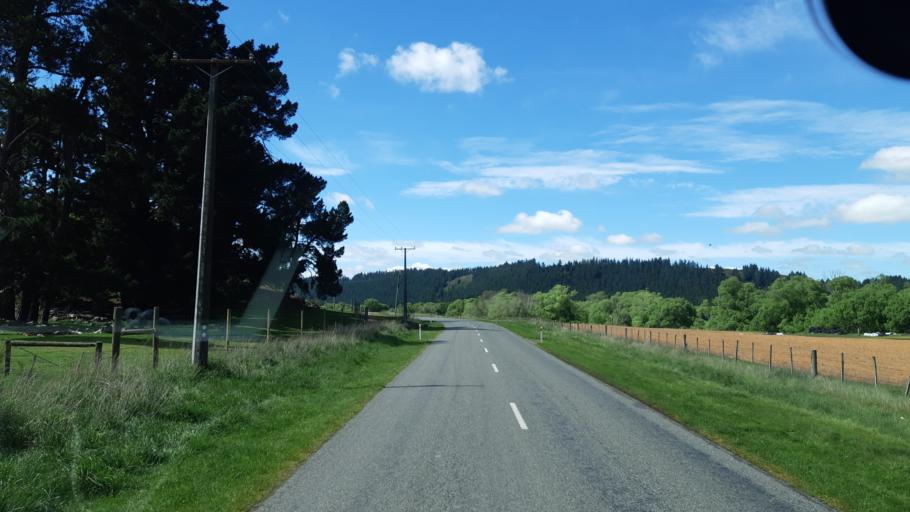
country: NZ
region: Canterbury
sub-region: Selwyn District
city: Darfield
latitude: -43.4775
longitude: 171.9149
